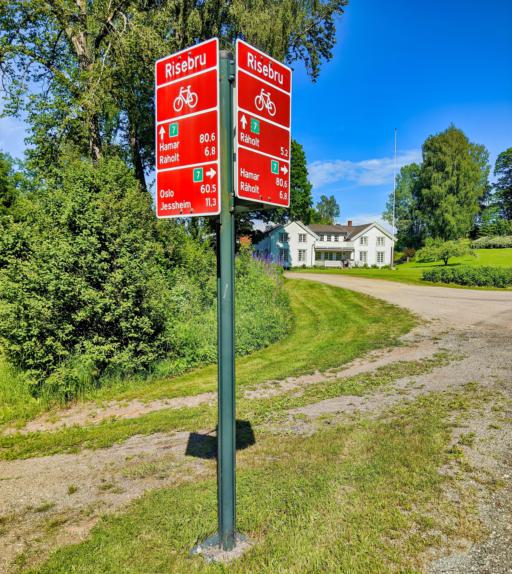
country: NO
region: Akershus
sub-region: Eidsvoll
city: Raholt
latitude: 60.2377
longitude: 11.1707
